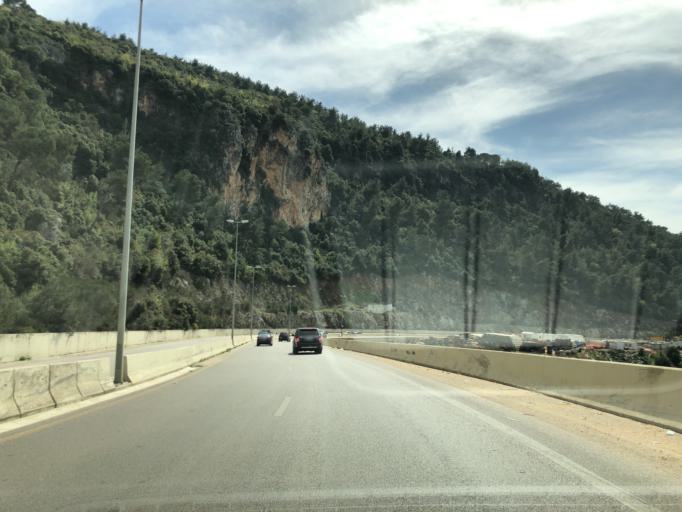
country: LB
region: Mont-Liban
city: Jdaidet el Matn
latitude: 33.9000
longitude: 35.6405
